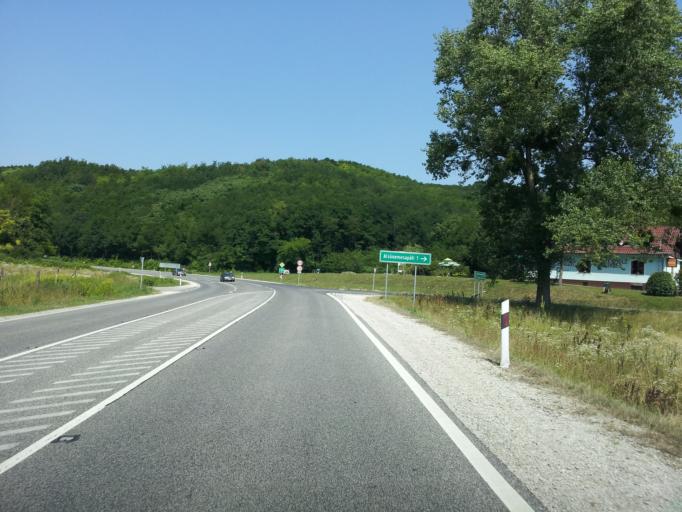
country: HU
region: Zala
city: Zalaegerszeg
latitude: 46.8466
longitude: 16.9225
